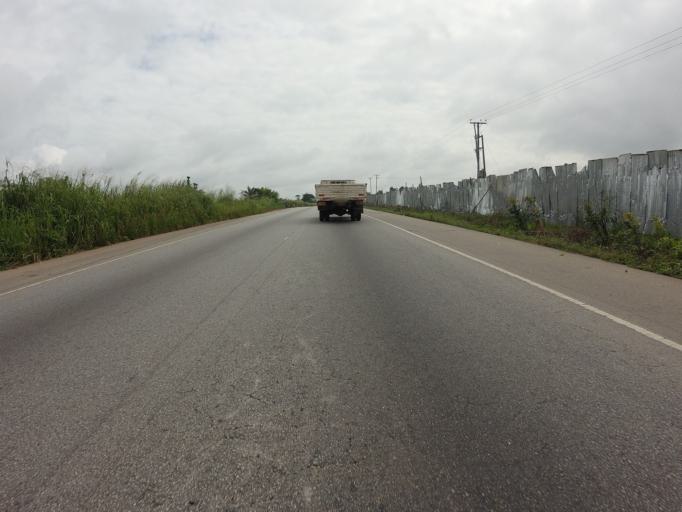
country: GH
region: Ashanti
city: Tafo
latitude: 6.9801
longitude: -1.6872
